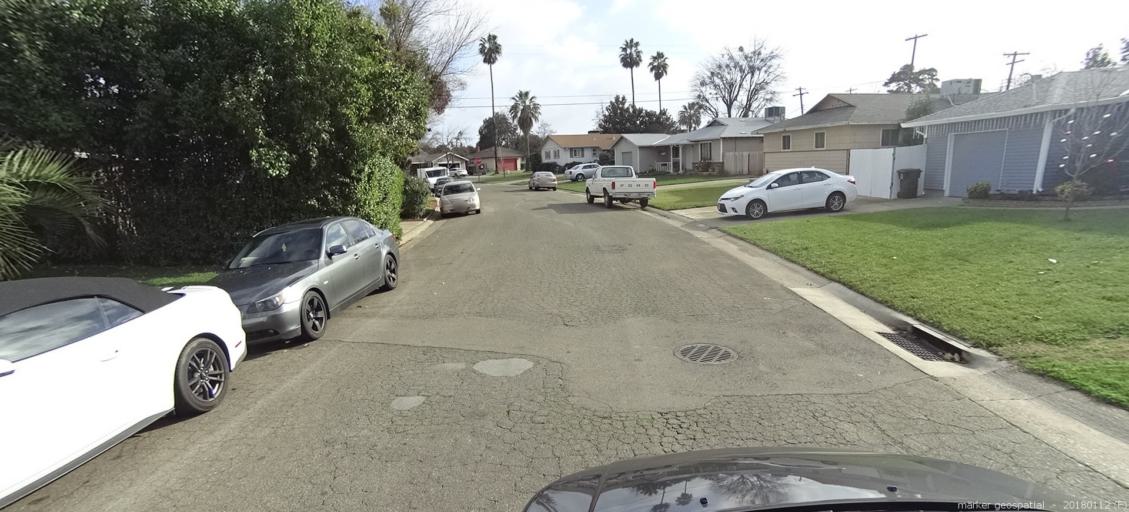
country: US
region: California
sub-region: Sacramento County
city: Rancho Cordova
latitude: 38.5956
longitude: -121.3004
